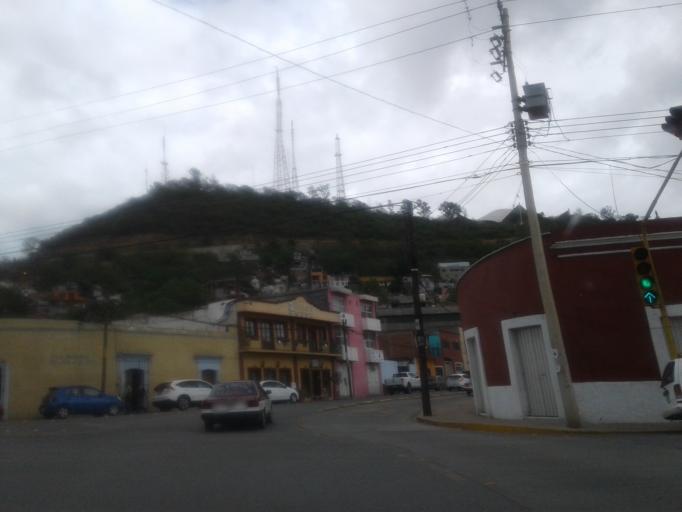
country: MX
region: Oaxaca
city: Oaxaca de Juarez
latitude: 17.0663
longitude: -96.7354
